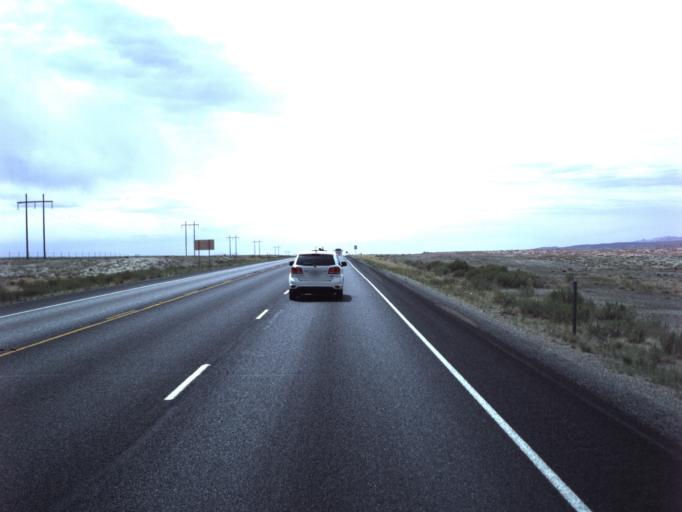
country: US
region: Utah
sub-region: Carbon County
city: East Carbon City
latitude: 39.1906
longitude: -110.3385
